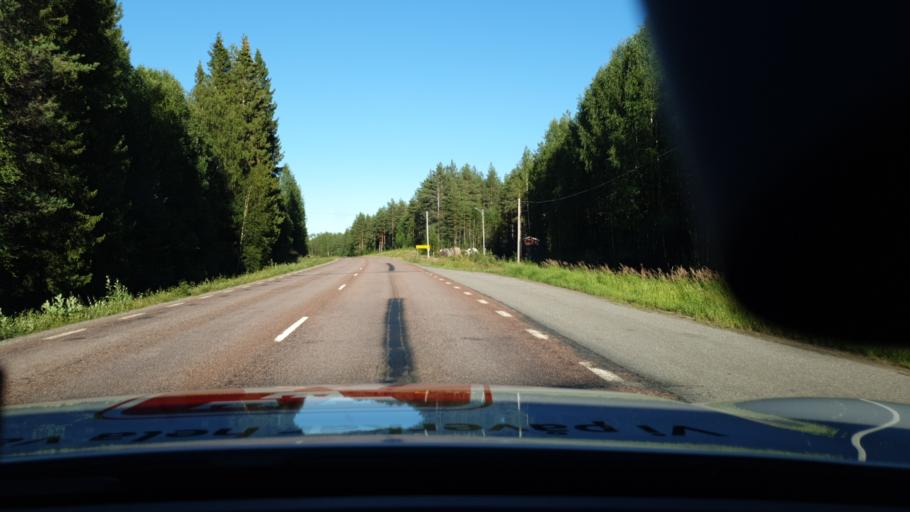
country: SE
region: Norrbotten
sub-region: Alvsbyns Kommun
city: AElvsbyn
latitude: 65.6712
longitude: 21.0888
